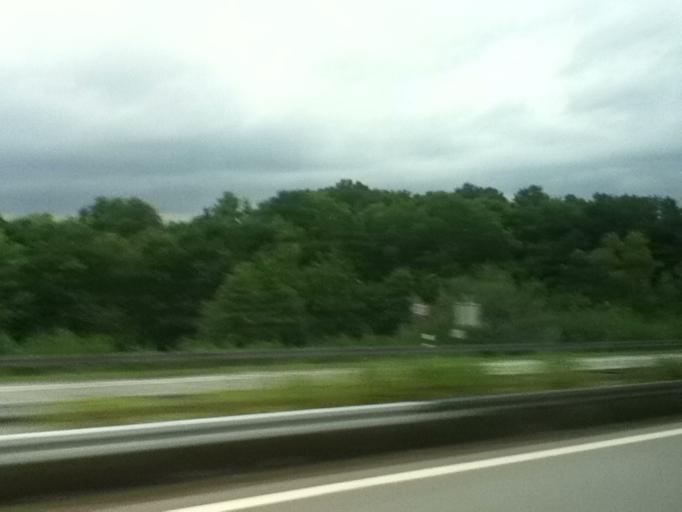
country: DE
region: Saxony
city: Pfaffroda
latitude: 50.8408
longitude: 12.5156
